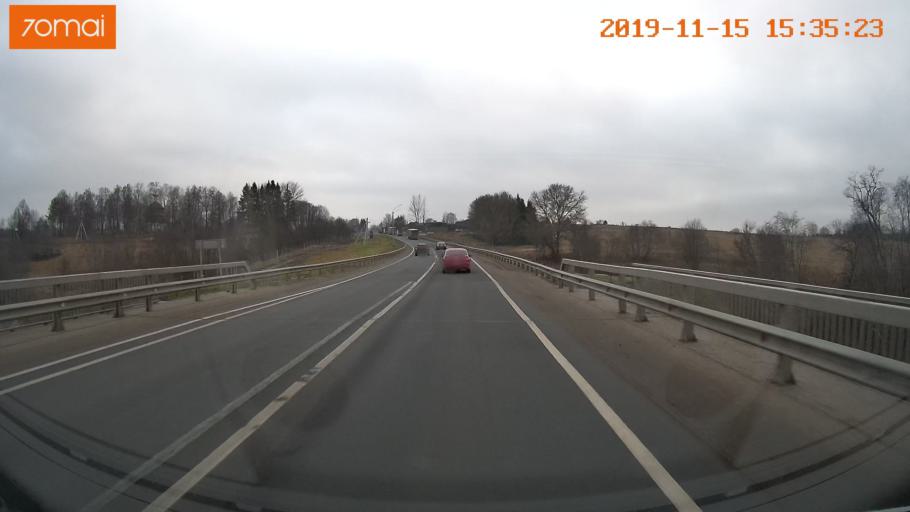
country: RU
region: Jaroslavl
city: Danilov
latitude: 58.0596
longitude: 40.0876
